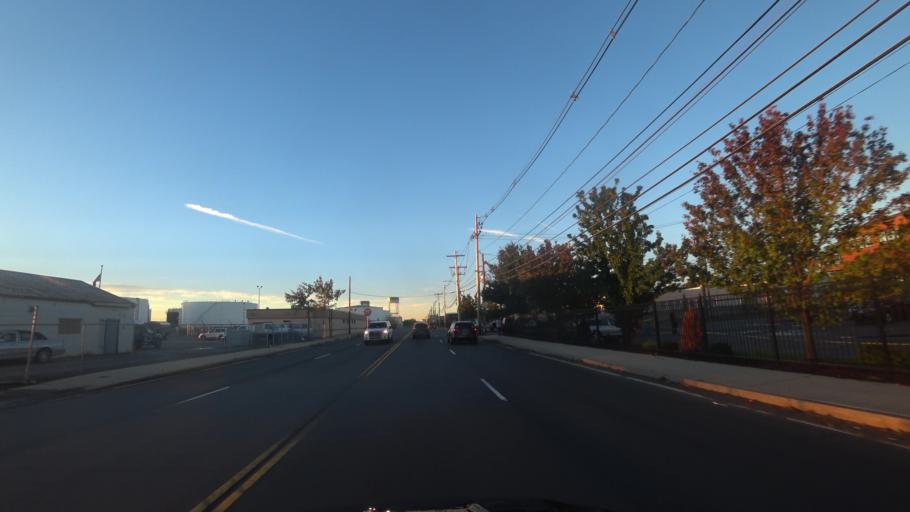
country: US
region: Massachusetts
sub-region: Suffolk County
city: Chelsea
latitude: 42.3957
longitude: -71.0212
